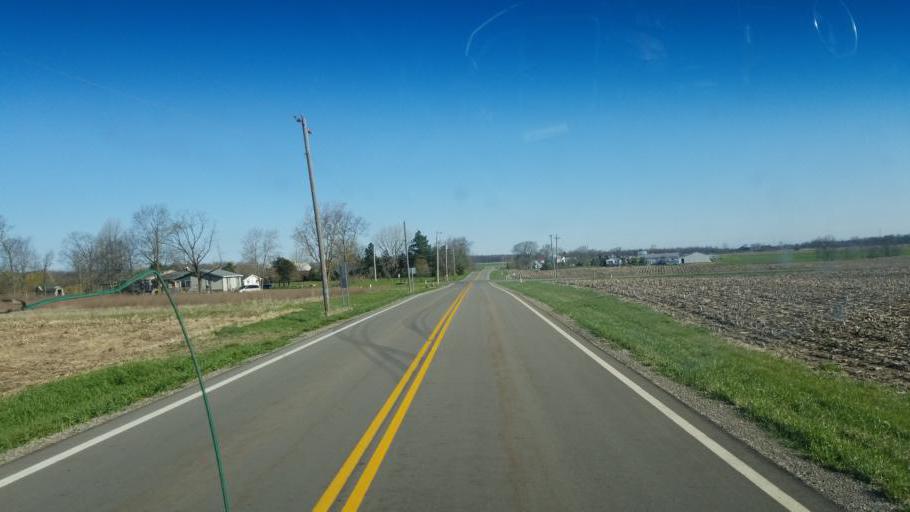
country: US
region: Ohio
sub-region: Logan County
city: Northwood
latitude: 40.4992
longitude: -83.6357
